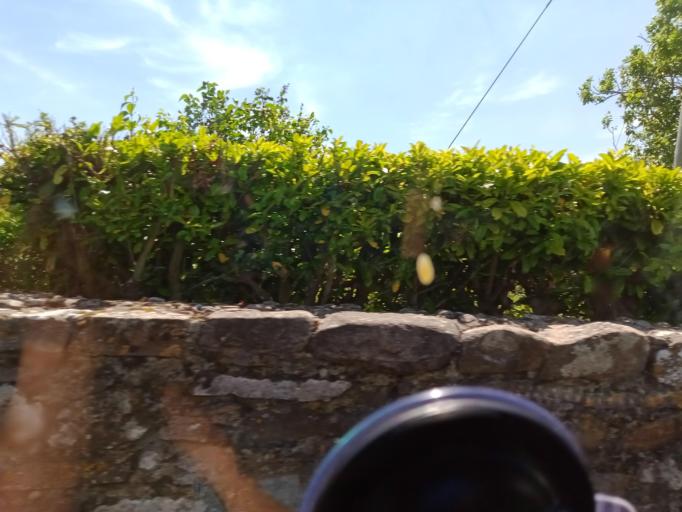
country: IE
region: Leinster
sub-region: Kilkenny
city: Thomastown
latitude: 52.5556
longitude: -7.1073
